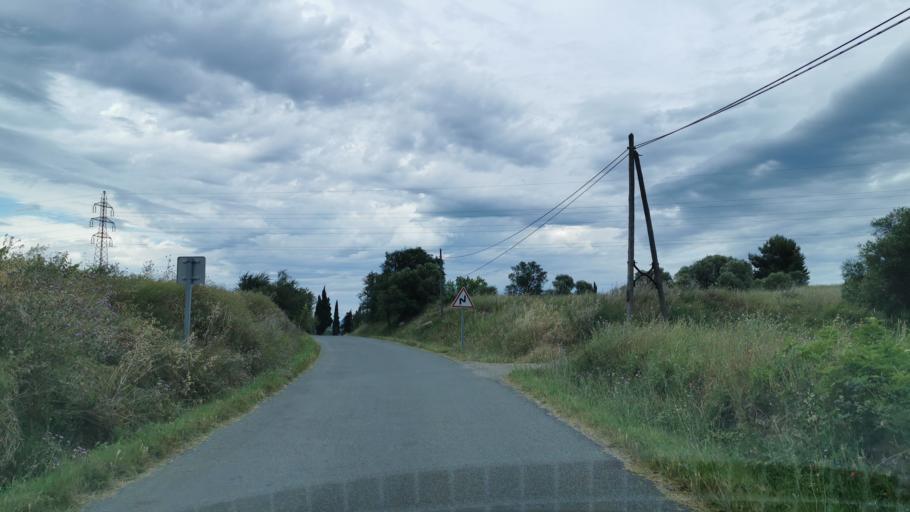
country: FR
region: Languedoc-Roussillon
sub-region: Departement de l'Aude
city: Moussan
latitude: 43.2352
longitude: 2.9551
